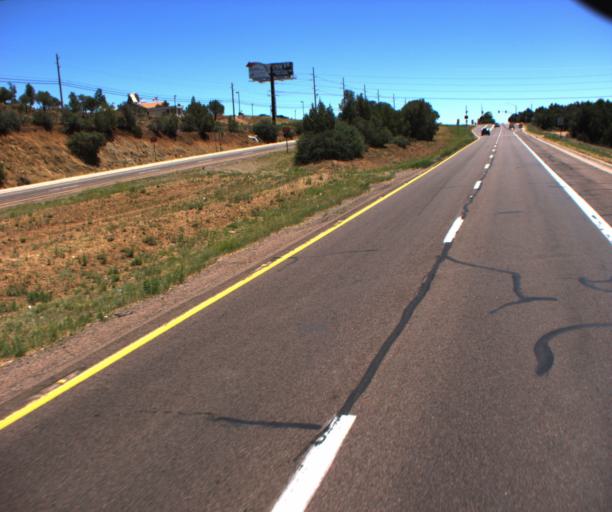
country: US
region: Arizona
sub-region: Gila County
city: Payson
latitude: 34.2226
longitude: -111.3325
